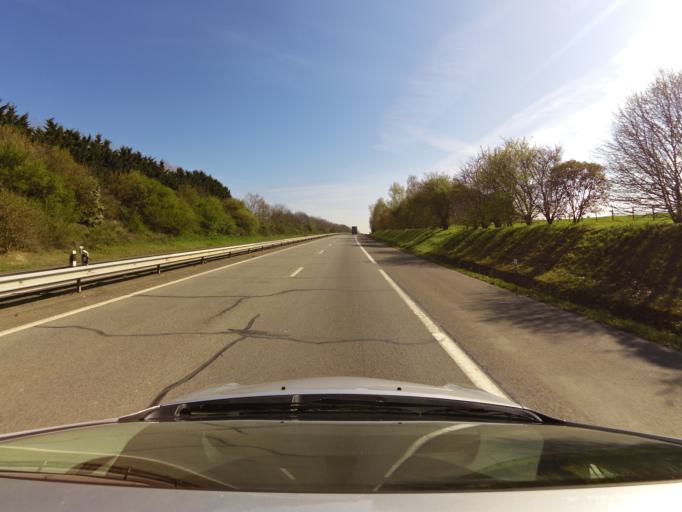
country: FR
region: Brittany
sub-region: Departement d'Ille-et-Vilaine
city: Le Rheu
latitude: 48.0916
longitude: -1.7735
